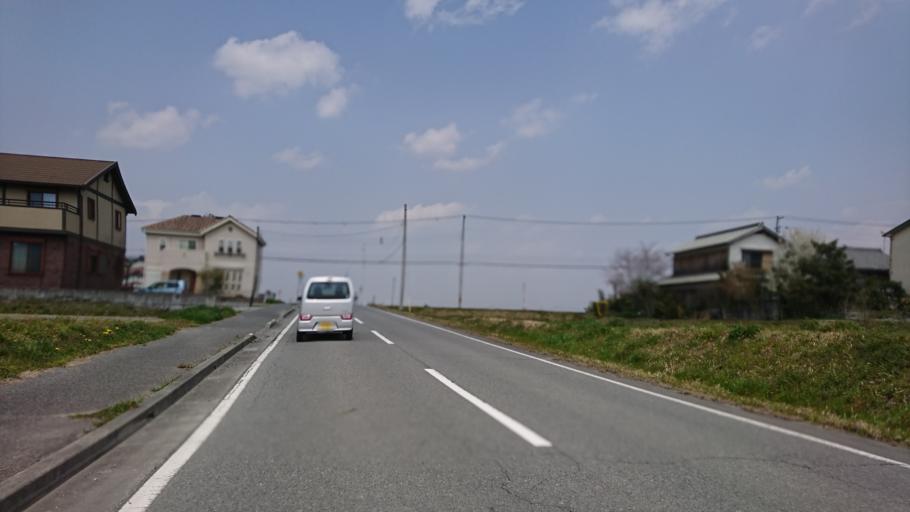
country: JP
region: Hyogo
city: Ono
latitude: 34.8363
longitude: 134.9103
